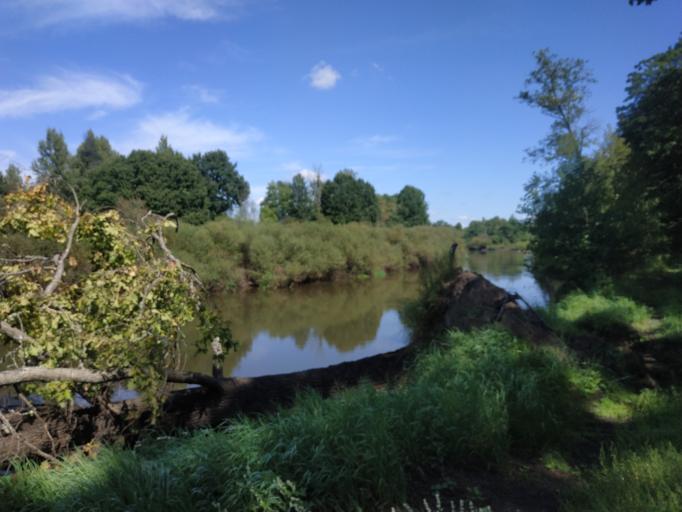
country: RU
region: Brjansk
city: Zhukovka
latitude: 53.5131
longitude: 33.6600
